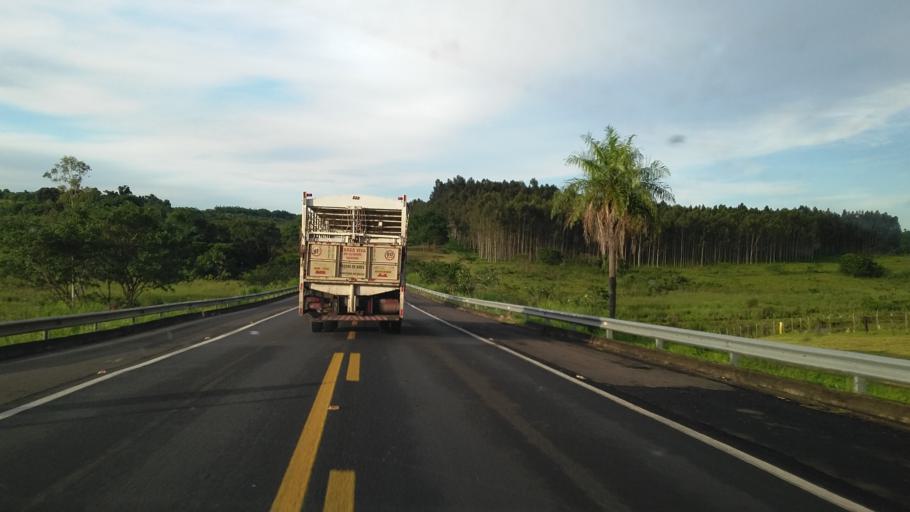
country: BR
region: Sao Paulo
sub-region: Marilia
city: Marilia
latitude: -21.9344
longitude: -49.9191
